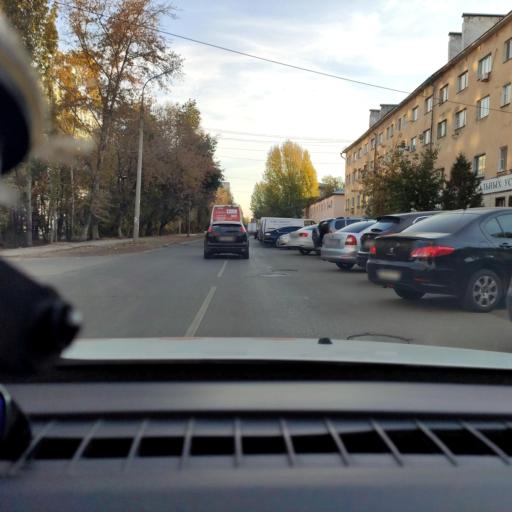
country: RU
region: Samara
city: Samara
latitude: 53.2087
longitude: 50.1803
